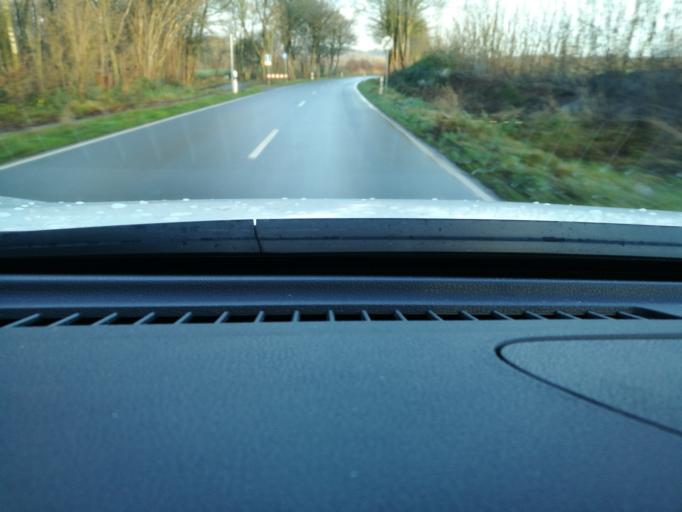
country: DE
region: Schleswig-Holstein
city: Holzbunge
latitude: 54.3867
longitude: 9.7068
